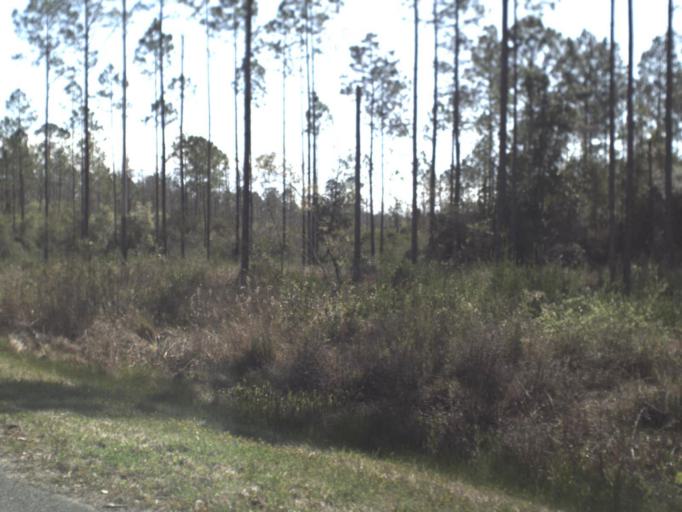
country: US
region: Florida
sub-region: Leon County
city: Woodville
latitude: 30.3426
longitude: -84.0098
